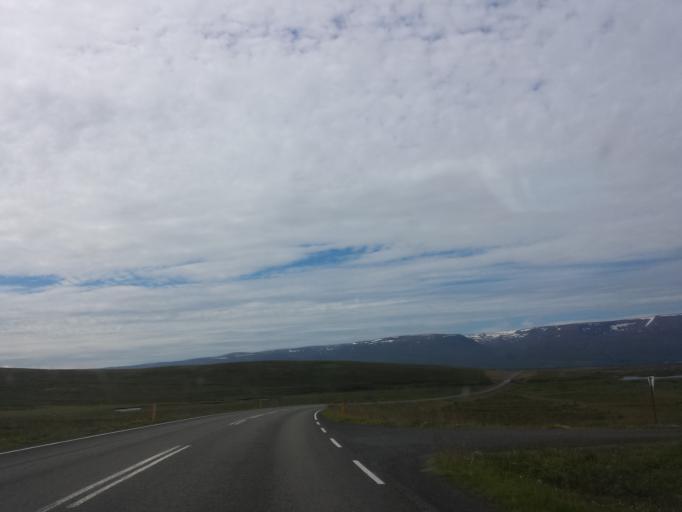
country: IS
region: Northeast
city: Husavik
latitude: 65.9705
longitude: -17.3852
